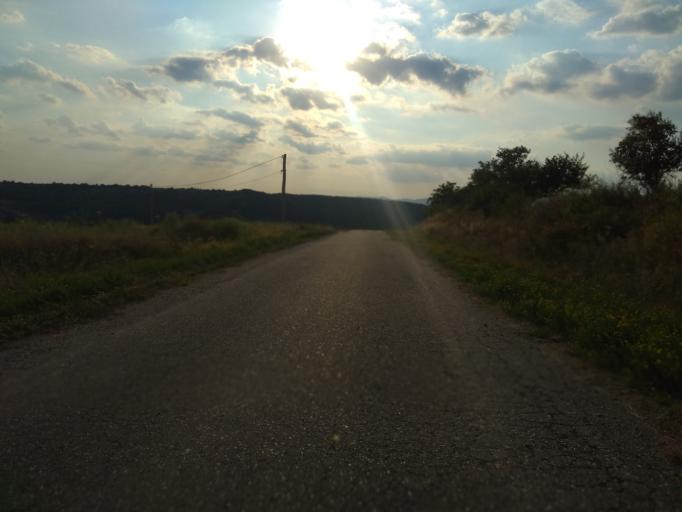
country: HU
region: Borsod-Abauj-Zemplen
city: Nyekladhaza
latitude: 47.9809
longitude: 20.7941
